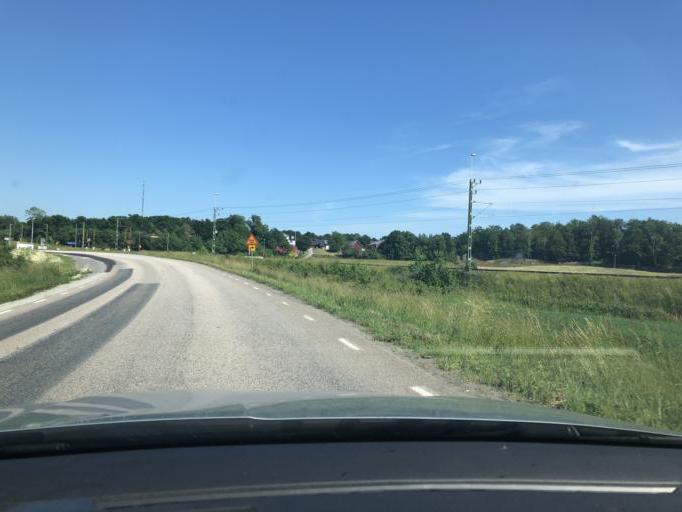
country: SE
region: Blekinge
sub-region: Karlshamns Kommun
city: Morrum
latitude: 56.1771
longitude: 14.7790
